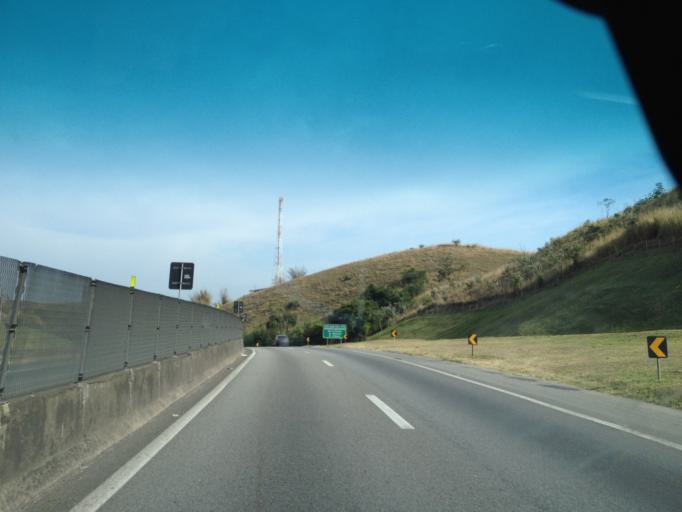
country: BR
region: Rio de Janeiro
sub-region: Barra Mansa
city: Barra Mansa
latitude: -22.5536
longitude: -44.1752
